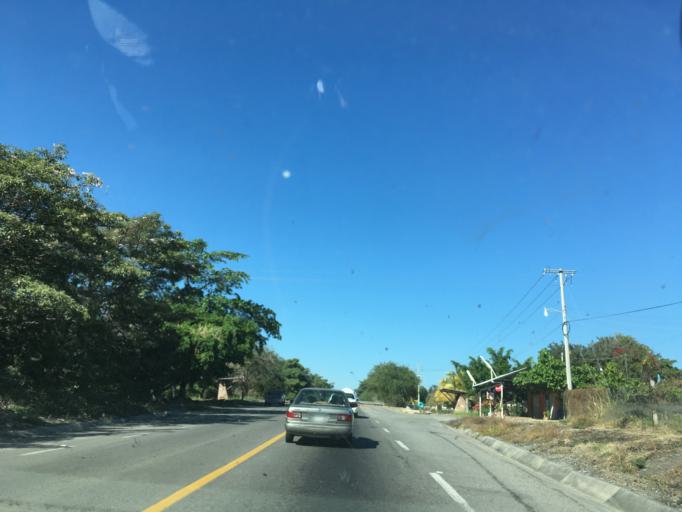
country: MX
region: Michoacan
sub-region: Gabriel Zamora
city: Lombardia
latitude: 19.0874
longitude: -102.0588
